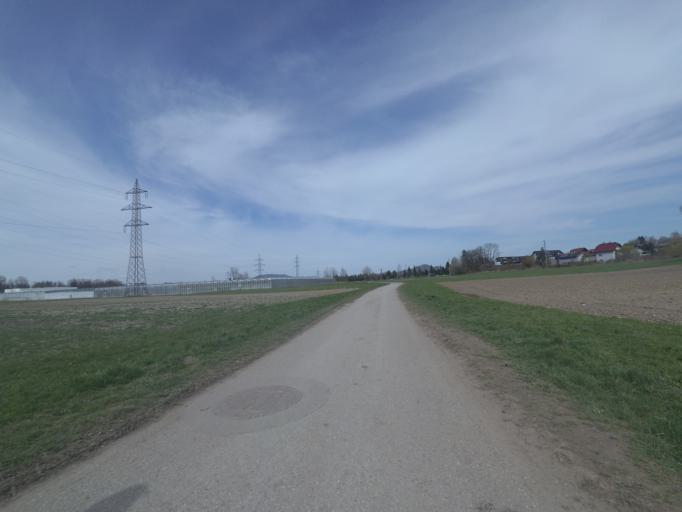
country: DE
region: Bavaria
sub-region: Upper Bavaria
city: Ainring
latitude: 47.8038
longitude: 12.9775
